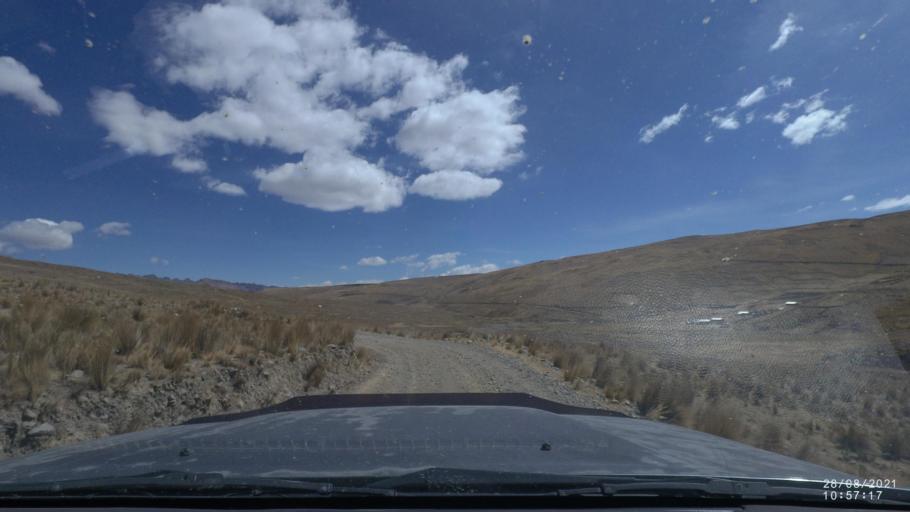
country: BO
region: Cochabamba
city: Cochabamba
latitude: -17.1888
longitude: -66.2508
